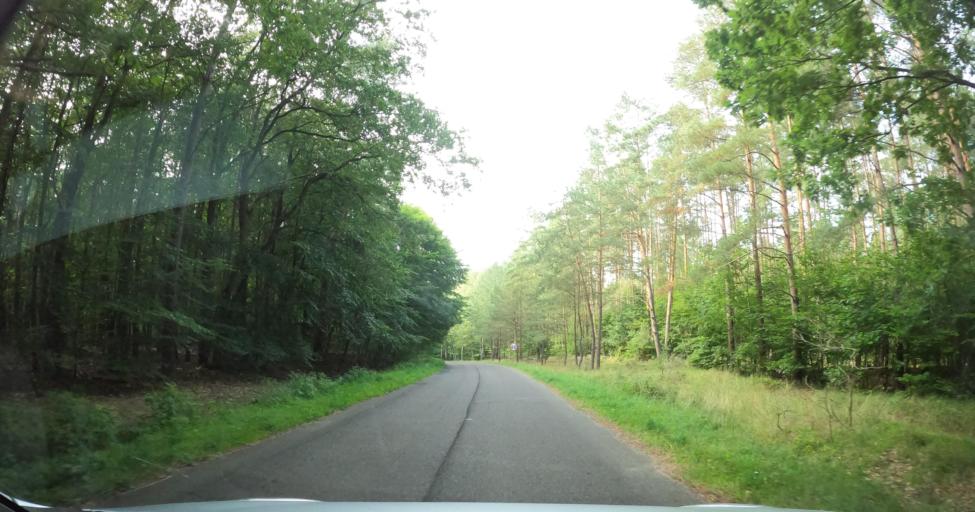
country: PL
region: West Pomeranian Voivodeship
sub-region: Powiat goleniowski
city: Goleniow
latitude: 53.5034
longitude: 14.8833
